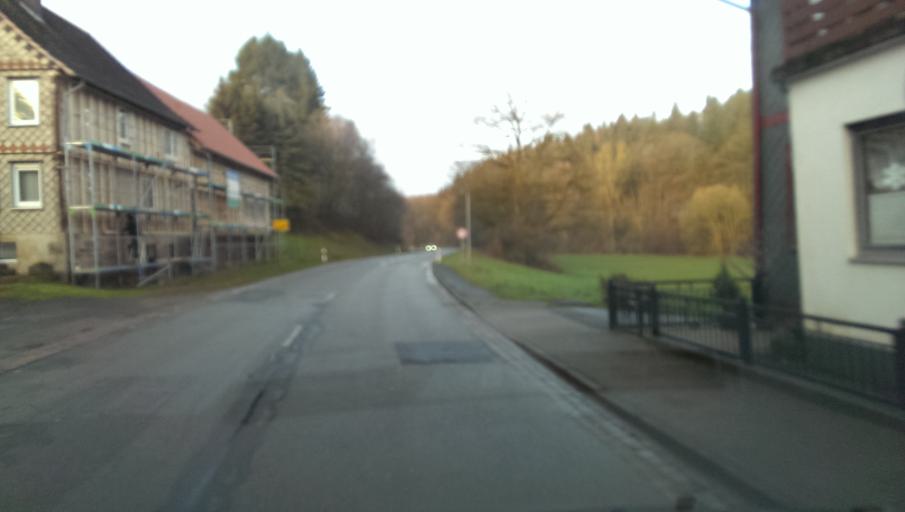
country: DE
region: Lower Saxony
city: Lenne
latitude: 51.8969
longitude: 9.6822
